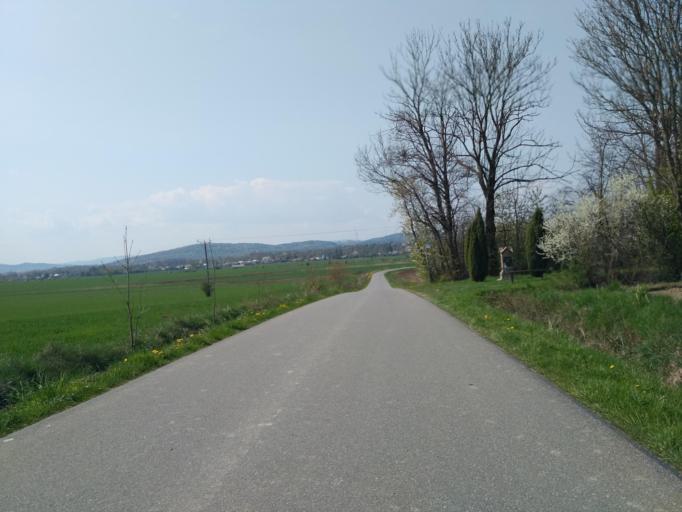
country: PL
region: Subcarpathian Voivodeship
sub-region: Krosno
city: Krosno
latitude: 49.6488
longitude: 21.7328
